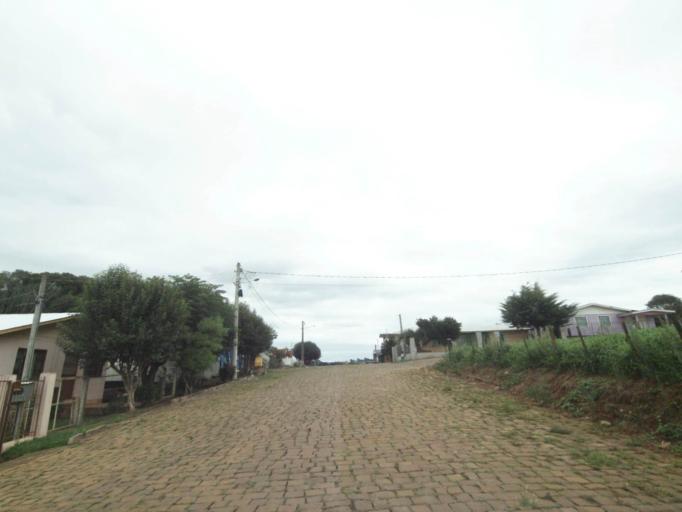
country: BR
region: Rio Grande do Sul
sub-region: Lagoa Vermelha
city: Lagoa Vermelha
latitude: -28.2116
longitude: -51.5049
